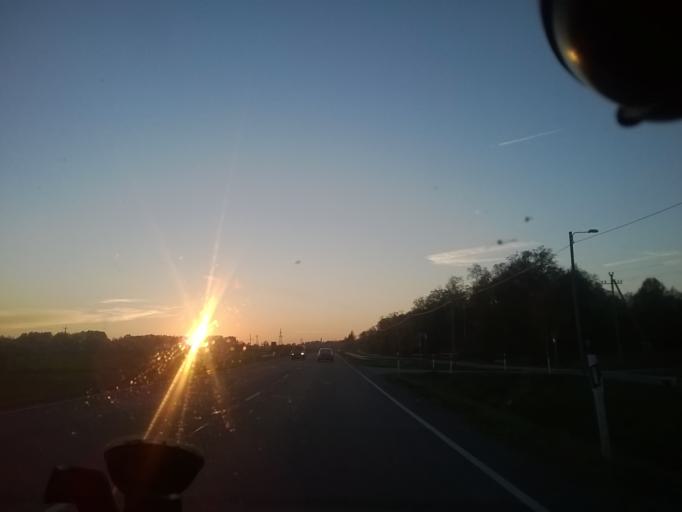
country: EE
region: Laeaene
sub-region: Ridala Parish
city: Uuemoisa
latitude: 58.9559
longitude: 23.7681
